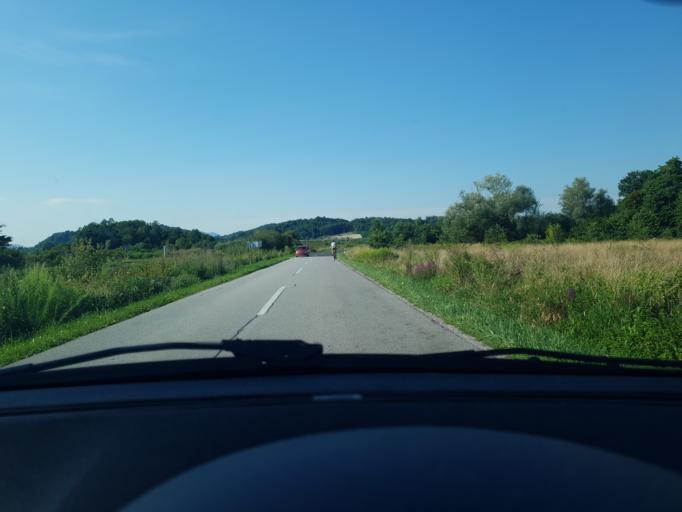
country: HR
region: Krapinsko-Zagorska
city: Oroslavje
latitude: 46.0078
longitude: 15.9309
